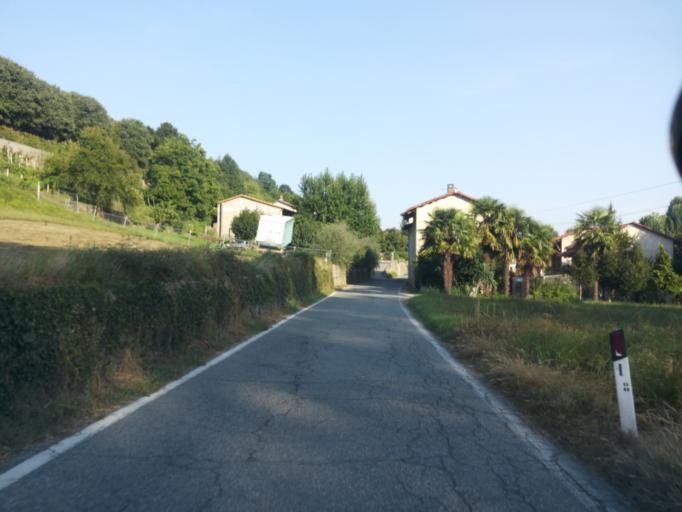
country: IT
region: Piedmont
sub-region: Provincia di Torino
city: Palazzo Canavese
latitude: 45.4640
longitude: 7.9667
